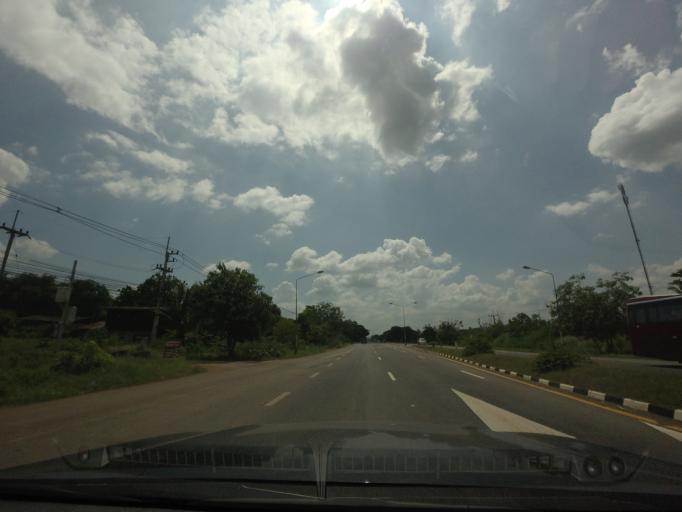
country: TH
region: Phetchabun
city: Nong Phai
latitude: 16.1625
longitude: 101.0709
